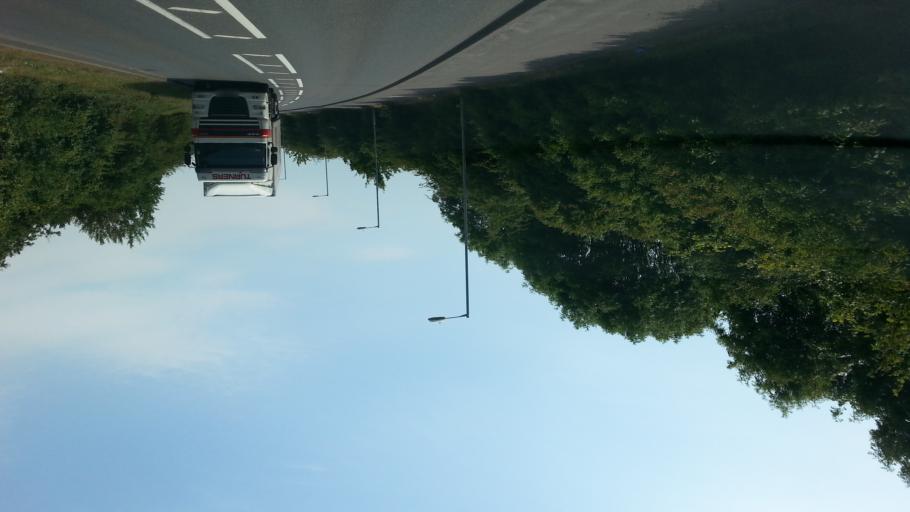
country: GB
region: England
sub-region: Cambridgeshire
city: Huntingdon
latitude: 52.3458
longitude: -0.1914
